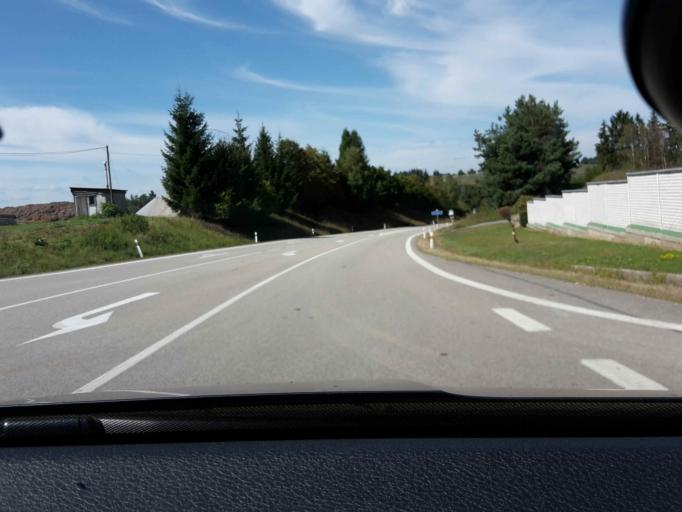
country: CZ
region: Jihocesky
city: Strmilov
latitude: 49.1551
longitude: 15.1969
